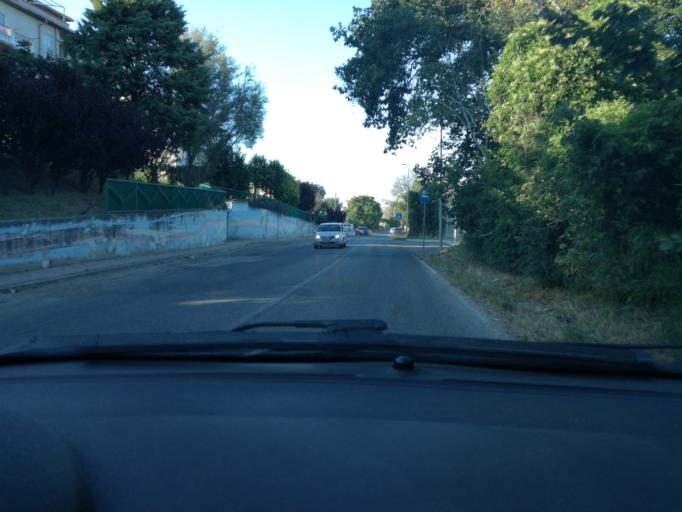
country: IT
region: Molise
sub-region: Provincia di Campobasso
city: Guglionesi
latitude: 41.9235
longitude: 14.9195
